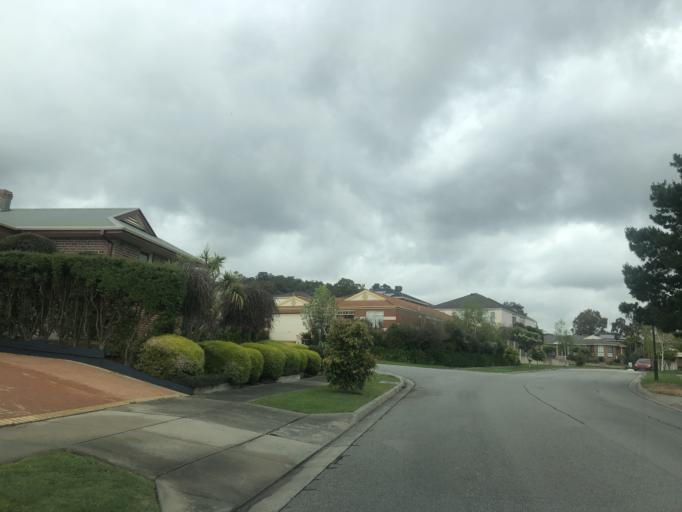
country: AU
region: Victoria
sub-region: Knox
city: Rowville
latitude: -37.9354
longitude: 145.2549
